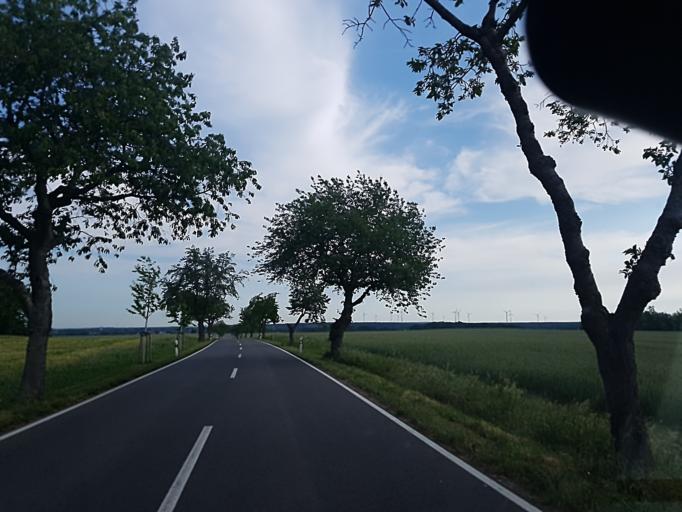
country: DE
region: Brandenburg
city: Niemegk
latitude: 52.0482
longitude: 12.6910
